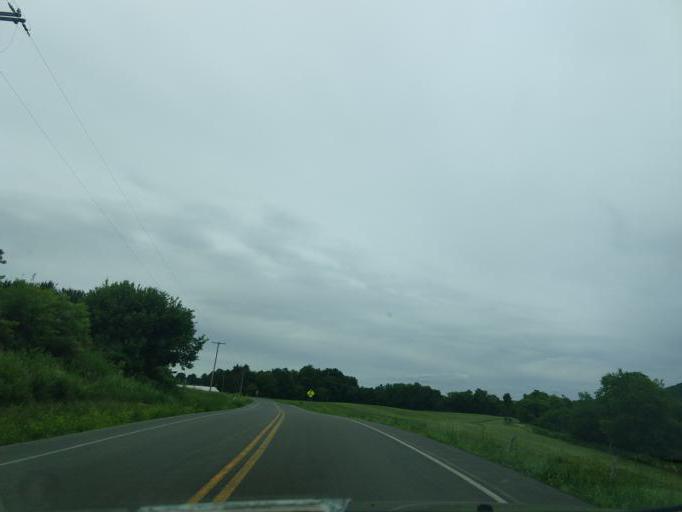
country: US
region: New York
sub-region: Tompkins County
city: Dryden
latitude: 42.4983
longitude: -76.2164
